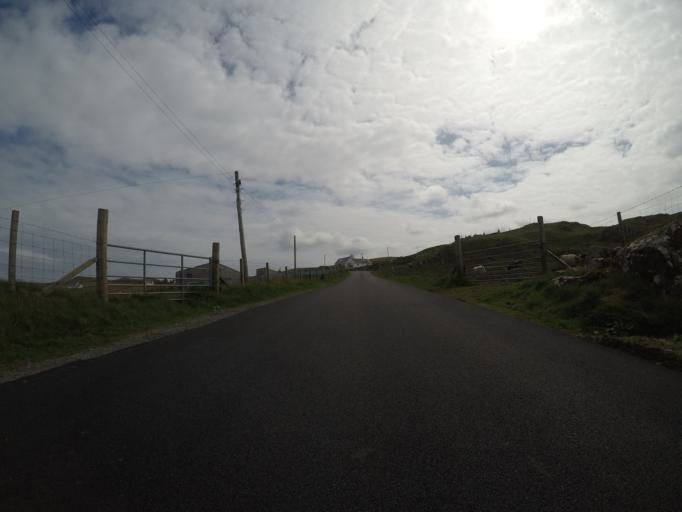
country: GB
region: Scotland
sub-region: Highland
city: Portree
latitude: 57.6836
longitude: -6.3005
